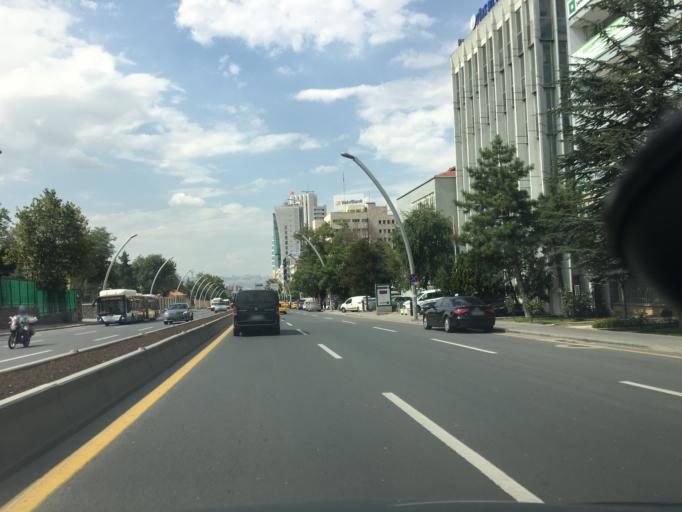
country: TR
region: Ankara
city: Cankaya
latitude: 39.9049
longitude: 32.8583
